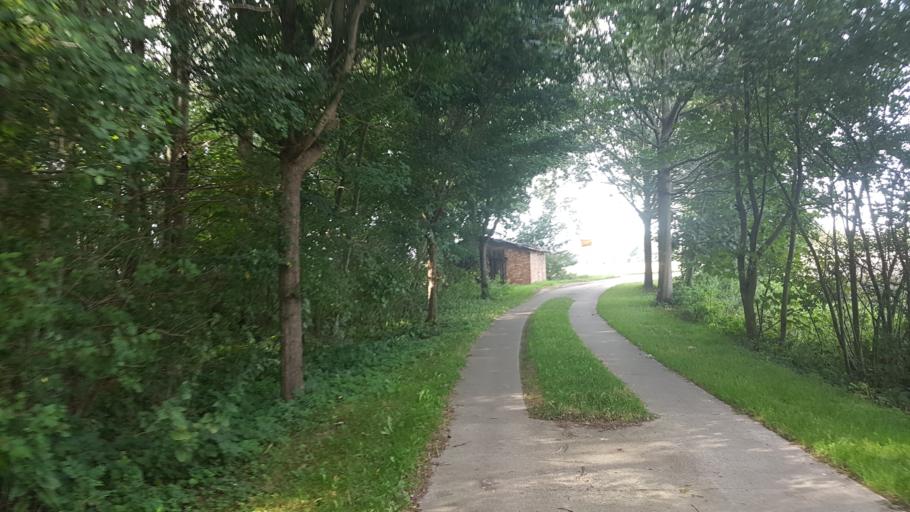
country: DE
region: Mecklenburg-Vorpommern
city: Gingst
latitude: 54.4424
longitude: 13.1846
